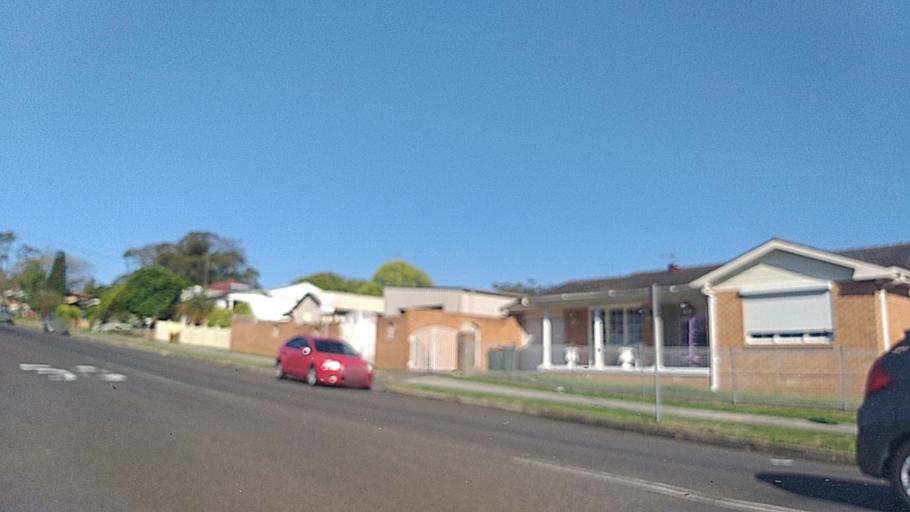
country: AU
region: New South Wales
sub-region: Wollongong
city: Koonawarra
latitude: -34.4851
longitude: 150.8047
